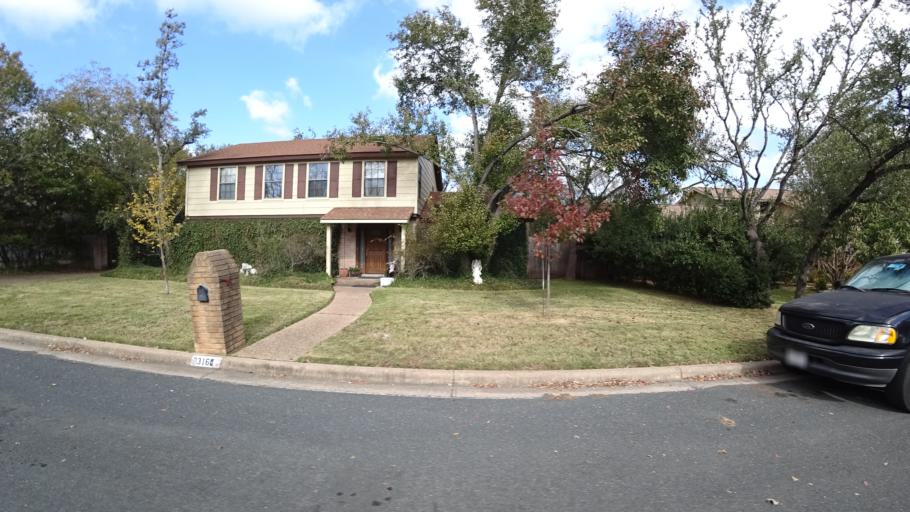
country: US
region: Texas
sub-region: Travis County
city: Shady Hollow
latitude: 30.1679
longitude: -97.8583
